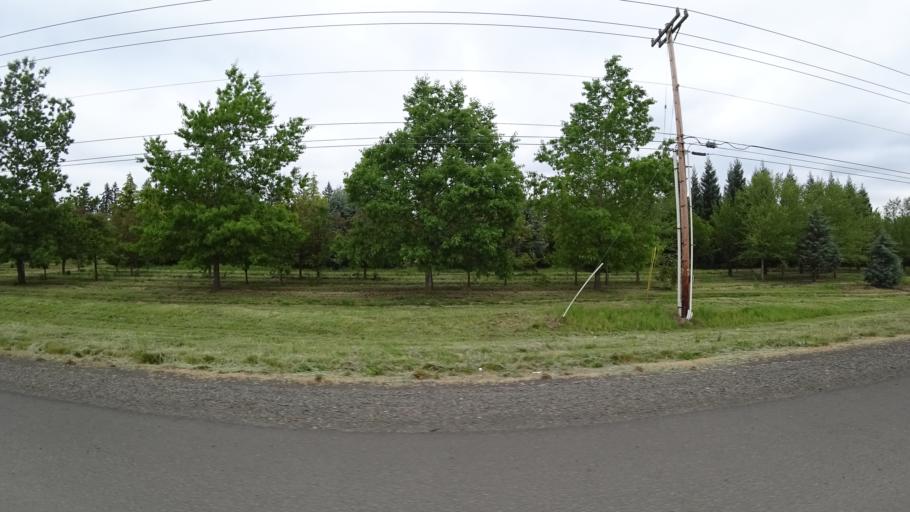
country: US
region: Oregon
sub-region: Washington County
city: Hillsboro
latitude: 45.4832
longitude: -122.9910
